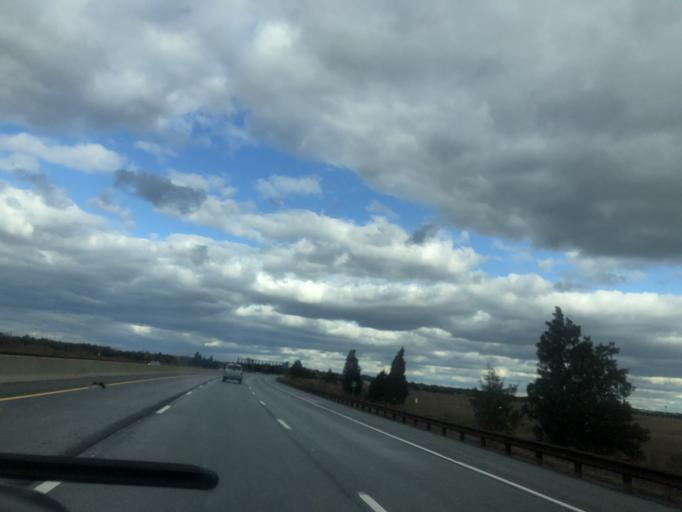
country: US
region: New Jersey
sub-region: Atlantic County
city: Port Republic
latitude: 39.5703
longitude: -74.4590
